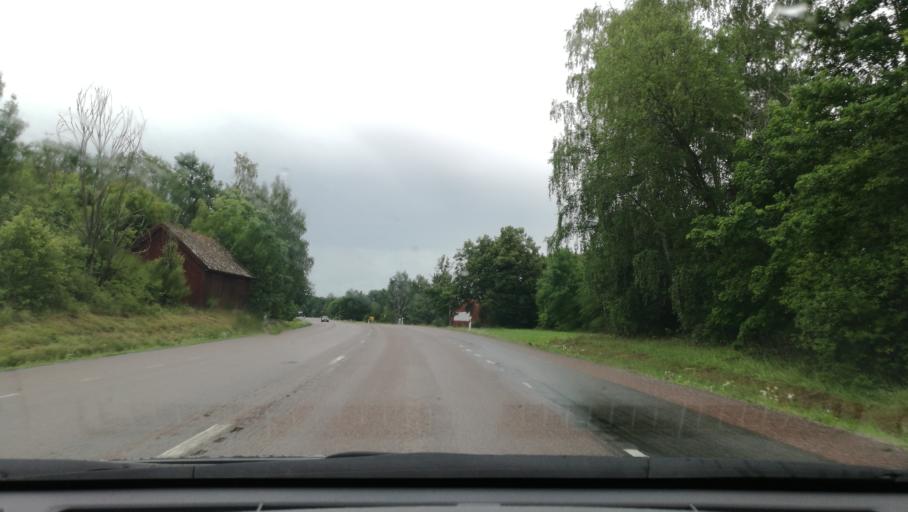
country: SE
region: Vaestmanland
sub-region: Kungsors Kommun
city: Kungsoer
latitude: 59.4430
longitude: 16.0458
